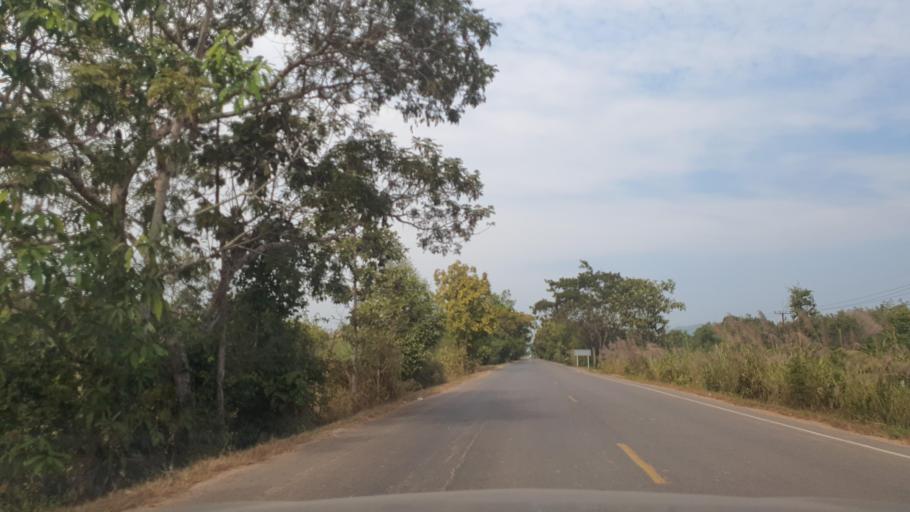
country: TH
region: Changwat Bueng Kan
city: Bung Khla
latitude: 18.1897
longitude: 104.0553
